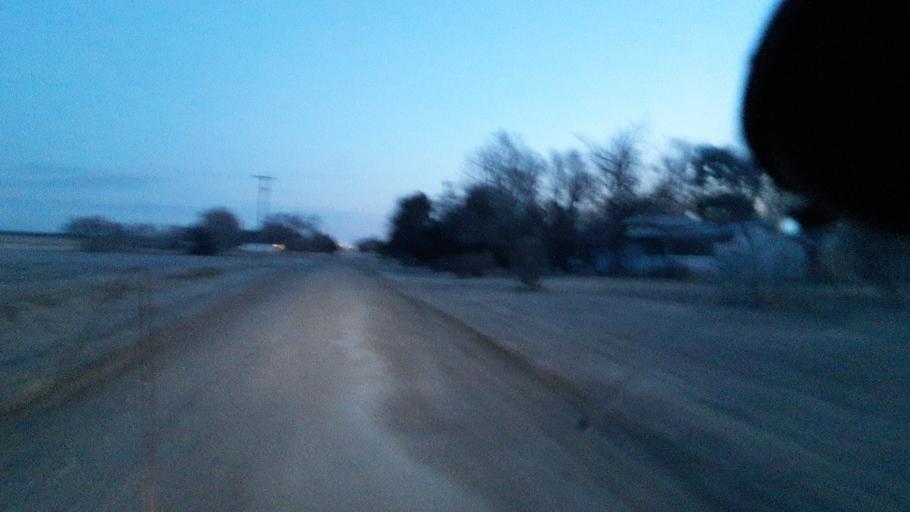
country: US
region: Kansas
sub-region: Reno County
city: South Hutchinson
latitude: 37.9992
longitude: -97.9772
